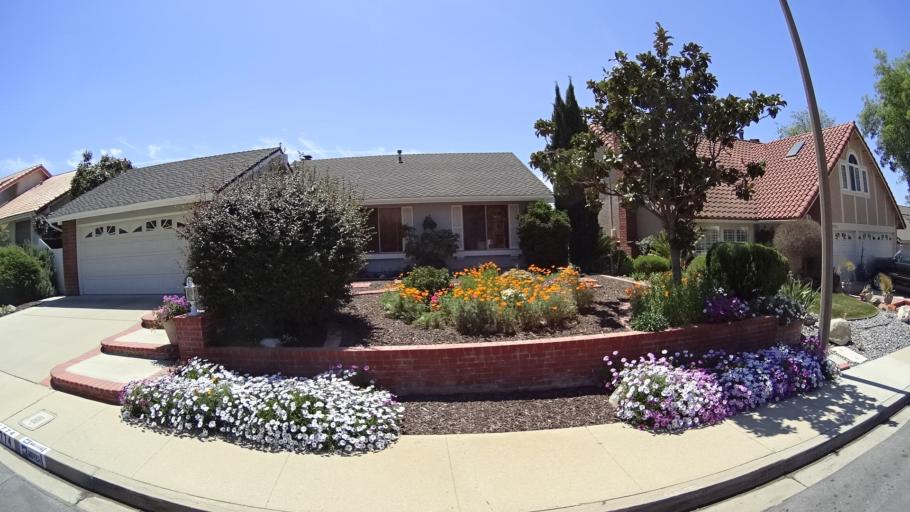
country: US
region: California
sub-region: Ventura County
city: Thousand Oaks
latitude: 34.2185
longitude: -118.8463
